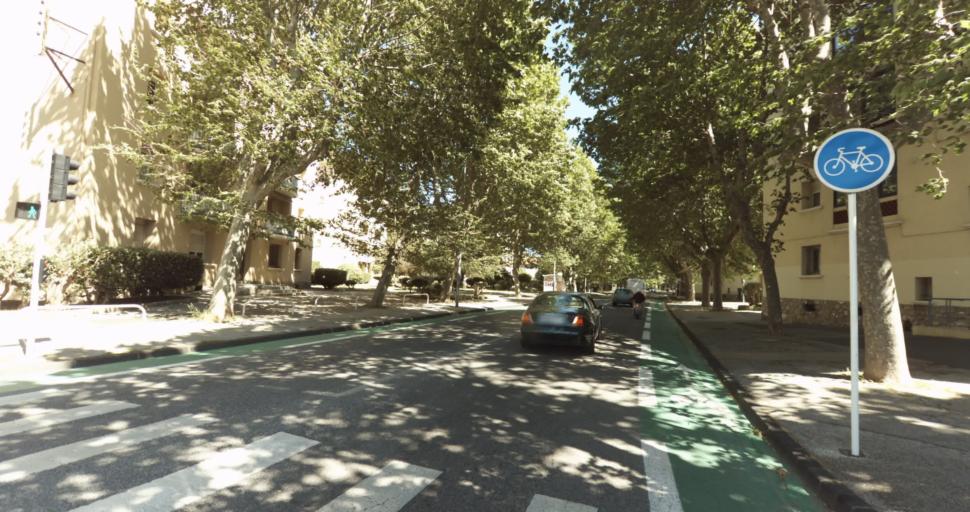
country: FR
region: Provence-Alpes-Cote d'Azur
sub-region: Departement du Var
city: Toulon
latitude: 43.1154
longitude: 5.9431
